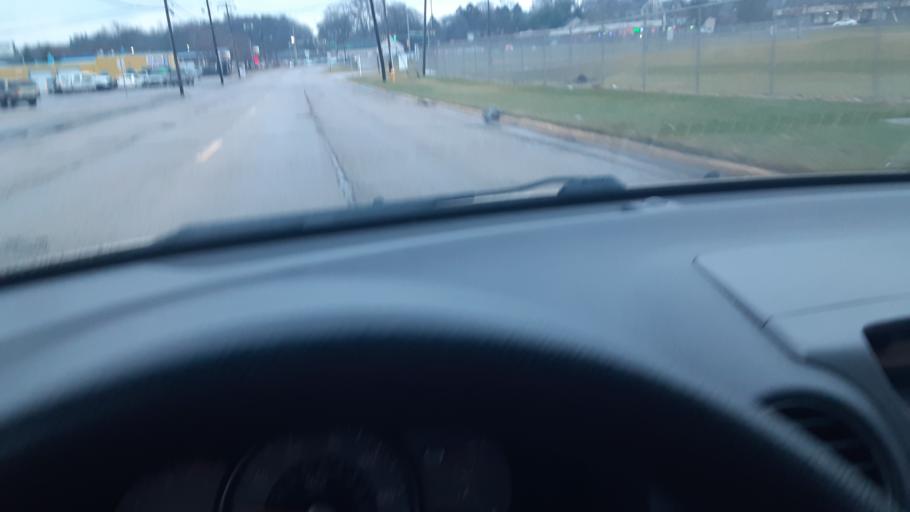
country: US
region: Illinois
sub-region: Winnebago County
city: Loves Park
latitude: 42.3107
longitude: -89.0440
